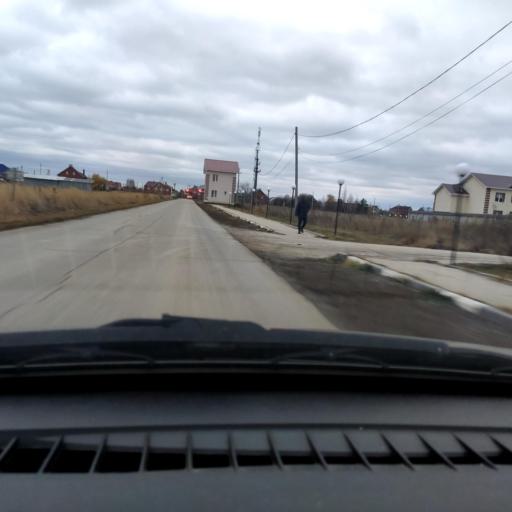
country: RU
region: Samara
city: Podstepki
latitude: 53.5241
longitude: 49.1843
